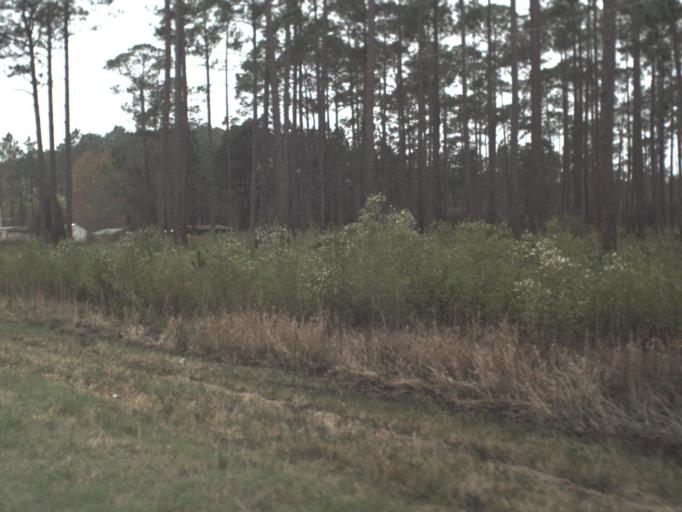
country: US
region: Florida
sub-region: Liberty County
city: Bristol
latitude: 30.3223
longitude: -84.8252
